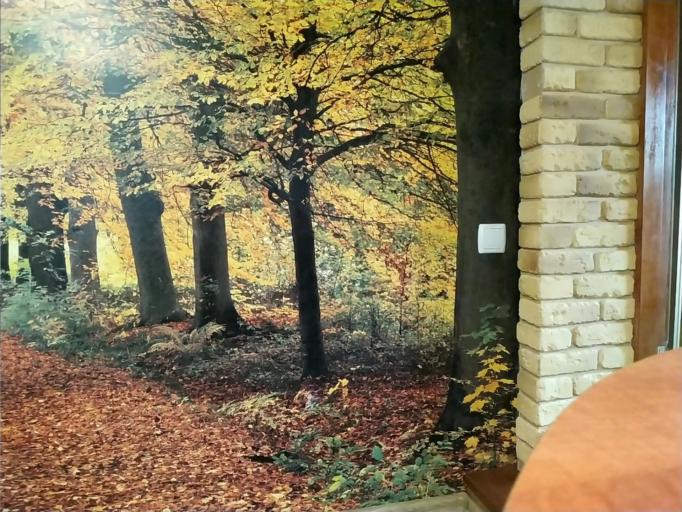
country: RU
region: Leningrad
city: Tolmachevo
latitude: 58.9349
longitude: 29.6990
